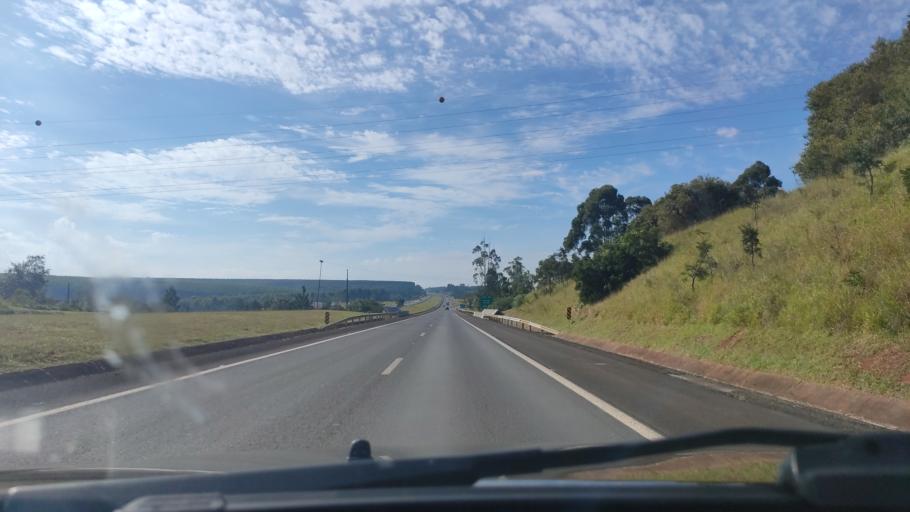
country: BR
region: Sao Paulo
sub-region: Itatinga
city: Itatinga
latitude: -23.0517
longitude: -48.5932
